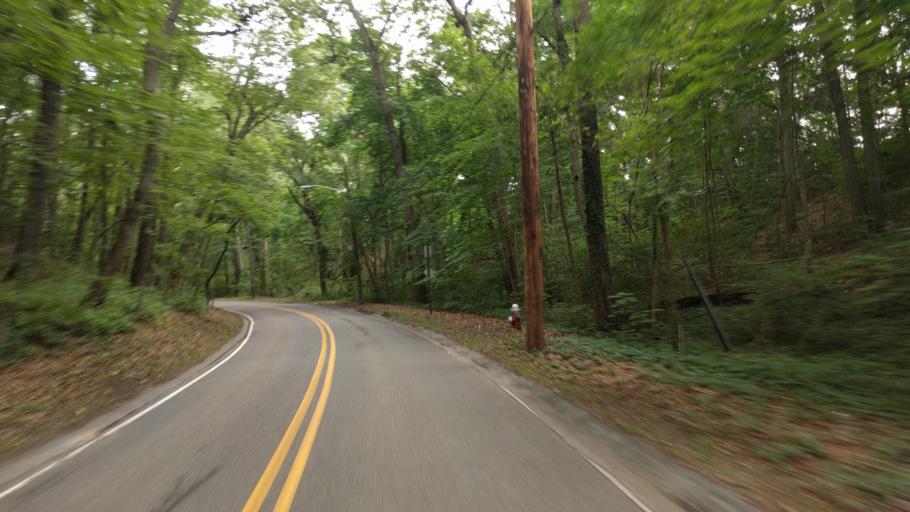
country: US
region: New York
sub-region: Nassau County
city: Oyster Bay Cove
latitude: 40.8650
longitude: -73.5168
